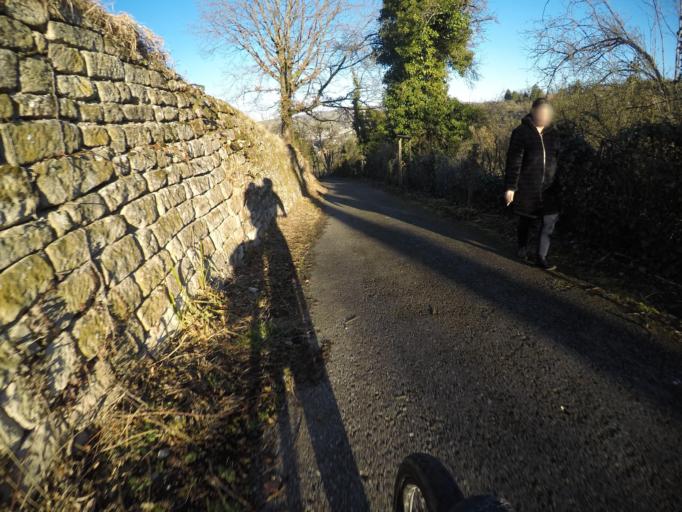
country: DE
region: Baden-Wuerttemberg
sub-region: Regierungsbezirk Stuttgart
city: Ostfildern
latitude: 48.7528
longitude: 9.2462
